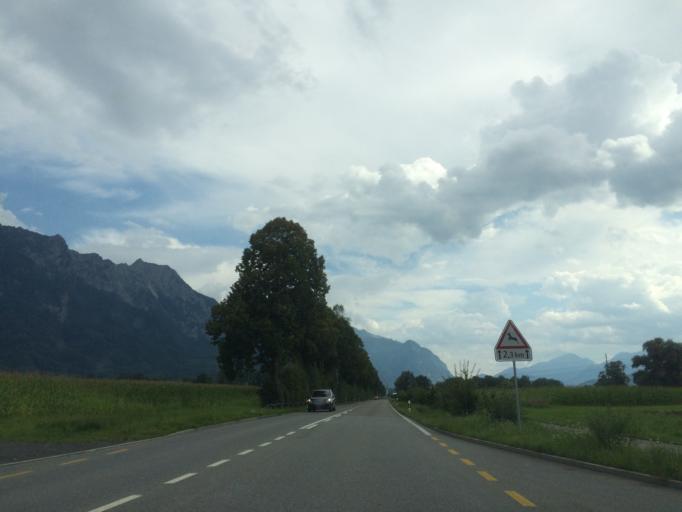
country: CH
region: Saint Gallen
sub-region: Wahlkreis Werdenberg
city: Haag (Rheintal)
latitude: 47.1980
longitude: 9.5017
